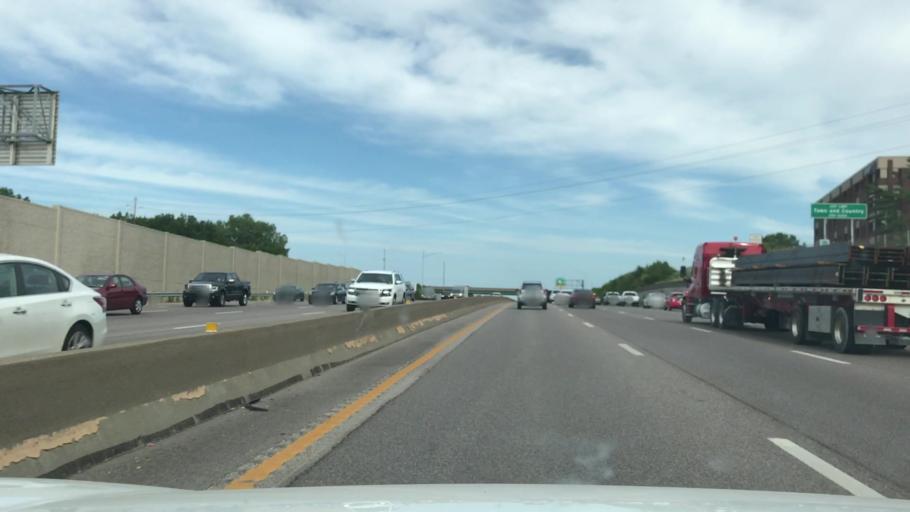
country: US
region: Missouri
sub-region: Saint Louis County
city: Manchester
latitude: 38.6442
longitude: -90.5185
